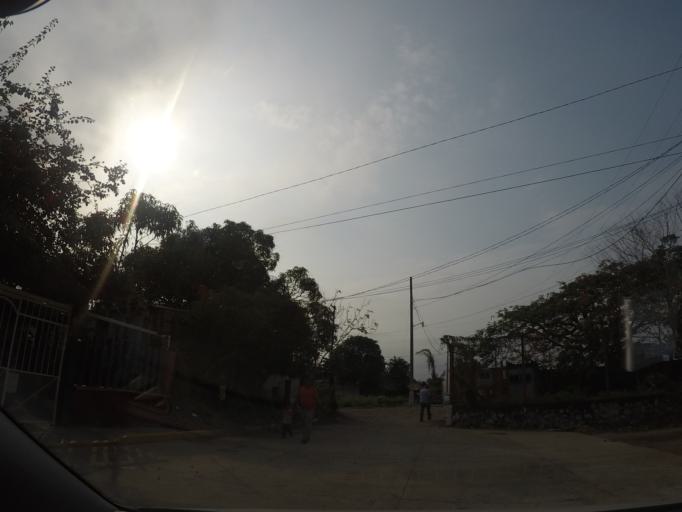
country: MX
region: Oaxaca
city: Matias Romero
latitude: 16.8838
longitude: -95.0413
